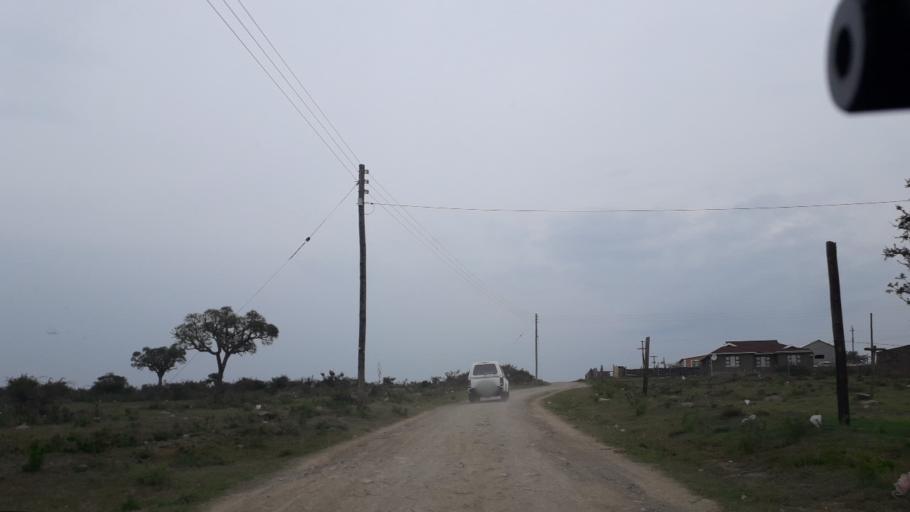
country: ZA
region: Eastern Cape
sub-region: Buffalo City Metropolitan Municipality
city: Bhisho
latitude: -32.8352
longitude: 27.3723
